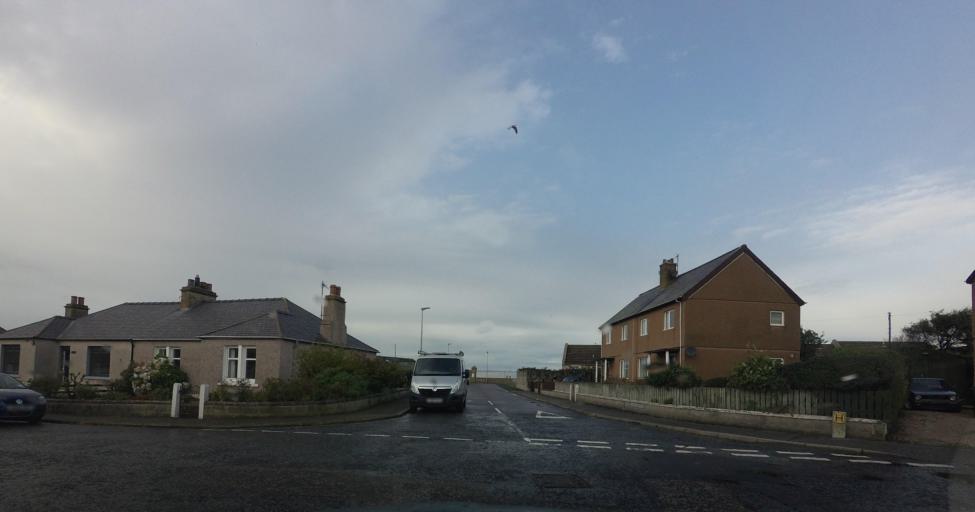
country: GB
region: Scotland
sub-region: Moray
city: Cullen
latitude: 57.6931
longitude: -2.8149
